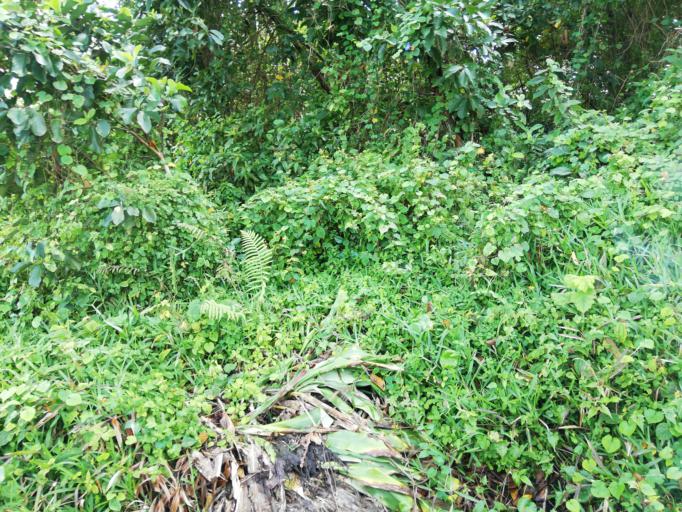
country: MU
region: Moka
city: Quartier Militaire
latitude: -20.2462
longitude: 57.5921
